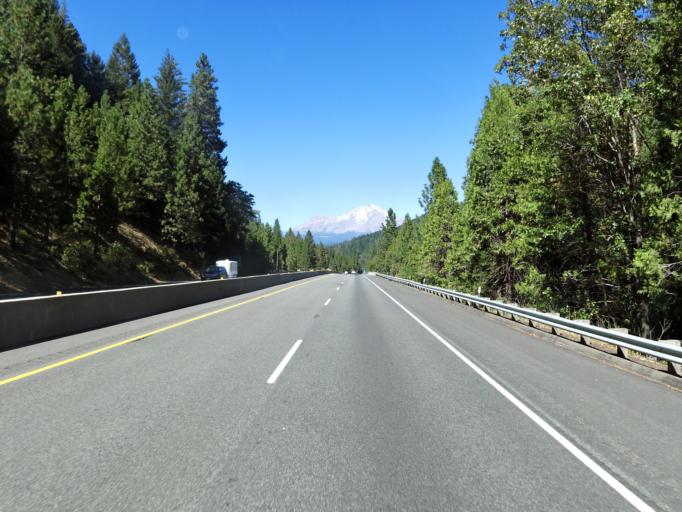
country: US
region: California
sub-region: Siskiyou County
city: Dunsmuir
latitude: 41.2064
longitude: -122.2768
